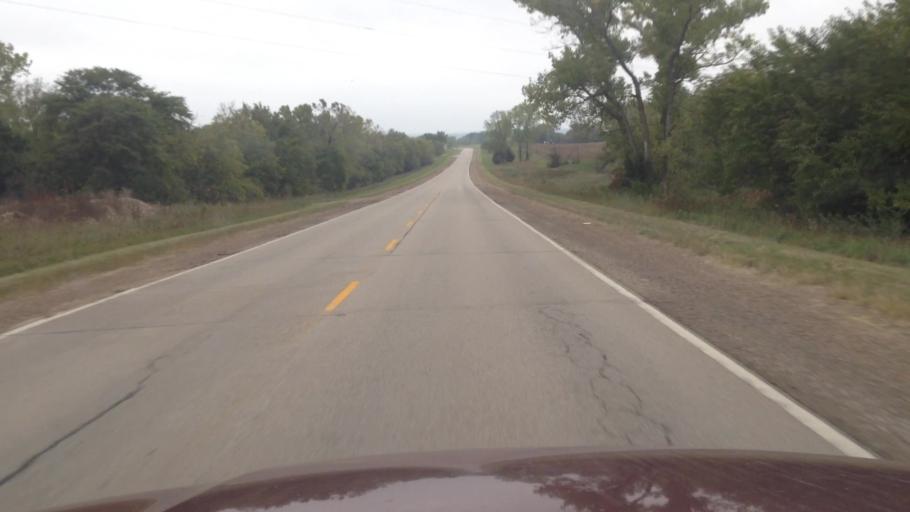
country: US
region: Kansas
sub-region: Jefferson County
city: Oskaloosa
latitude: 39.1130
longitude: -95.4837
